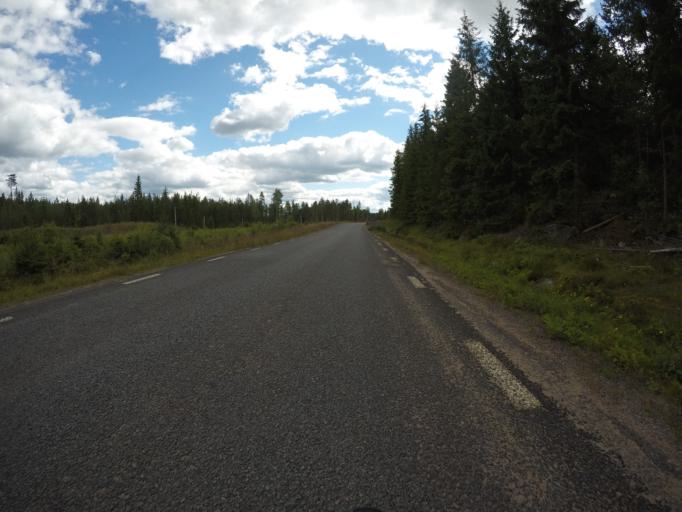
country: SE
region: OErebro
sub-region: Hallefors Kommun
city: Haellefors
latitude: 60.0807
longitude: 14.4840
